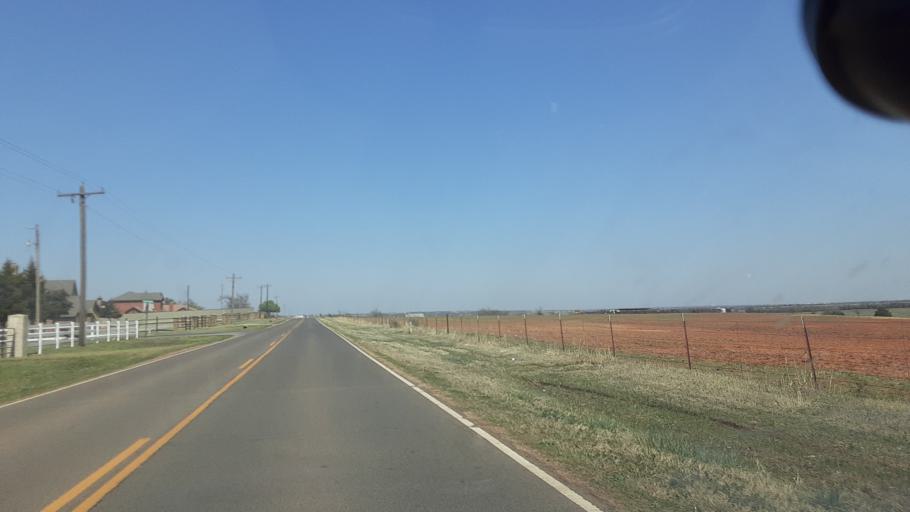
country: US
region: Oklahoma
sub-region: Logan County
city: Guthrie
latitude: 35.7880
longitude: -97.4783
